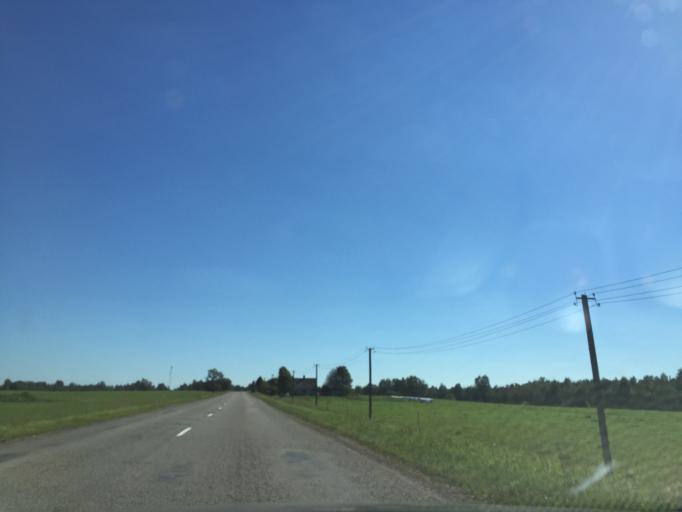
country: LV
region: Akniste
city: Akniste
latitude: 56.0638
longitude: 25.8953
